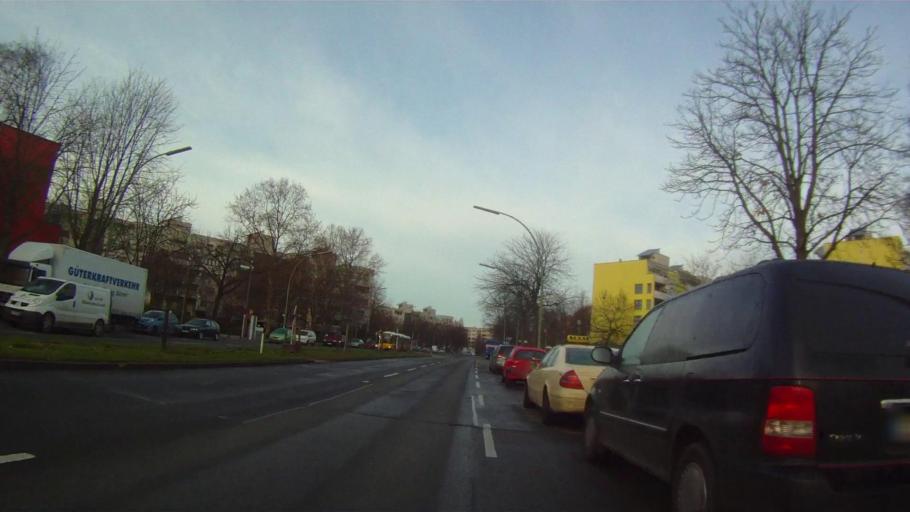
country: DE
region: Berlin
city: Baumschulenweg
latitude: 52.4621
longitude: 13.4776
